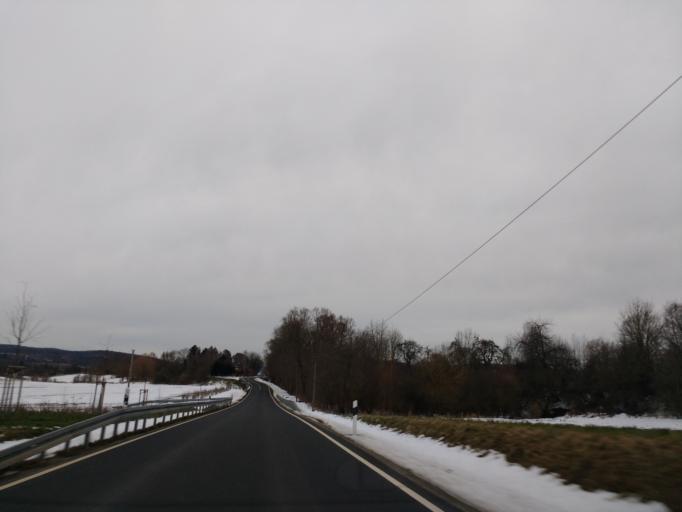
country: DE
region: Thuringia
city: Hohengandern
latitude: 51.3869
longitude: 9.9399
